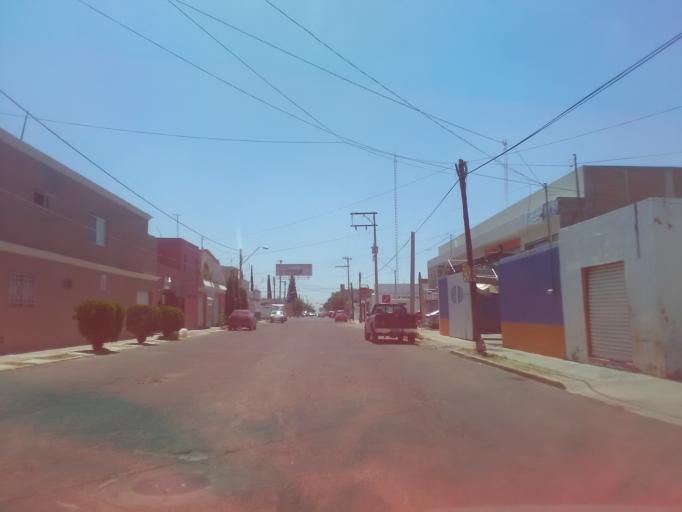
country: MX
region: Durango
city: Victoria de Durango
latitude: 24.0125
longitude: -104.6803
